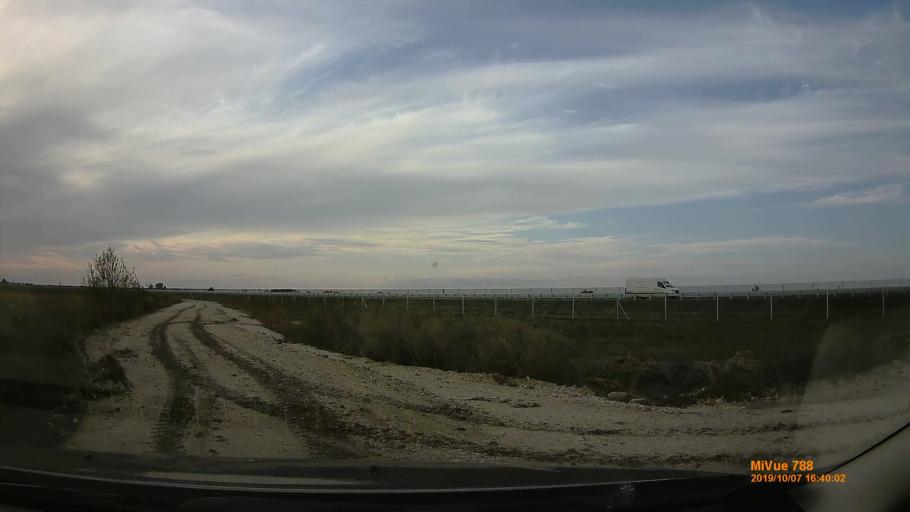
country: HU
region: Bekes
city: Szarvas
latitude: 46.8188
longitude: 20.5982
